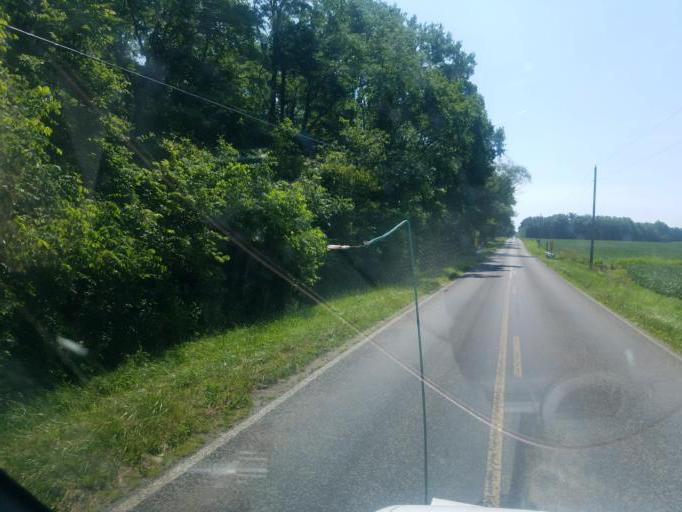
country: US
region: Ohio
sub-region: Champaign County
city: North Lewisburg
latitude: 40.2227
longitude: -83.5212
